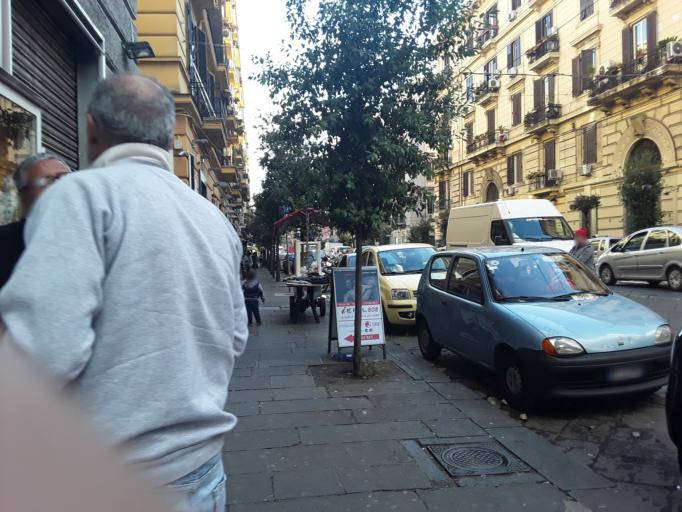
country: IT
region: Campania
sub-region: Provincia di Napoli
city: Napoli
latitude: 40.8574
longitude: 14.2673
